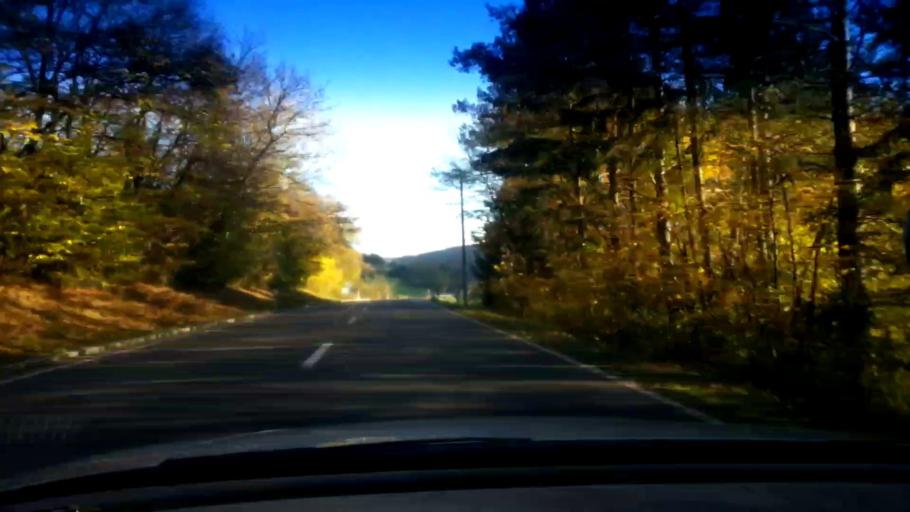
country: DE
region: Bavaria
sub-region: Upper Franconia
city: Heiligenstadt
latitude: 49.8566
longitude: 11.1790
